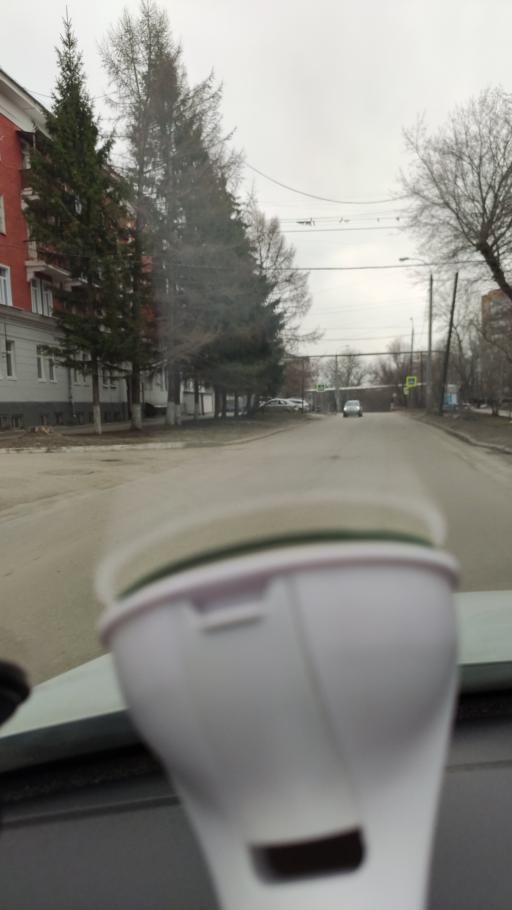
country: RU
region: Samara
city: Volzhskiy
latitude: 53.3442
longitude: 50.2162
